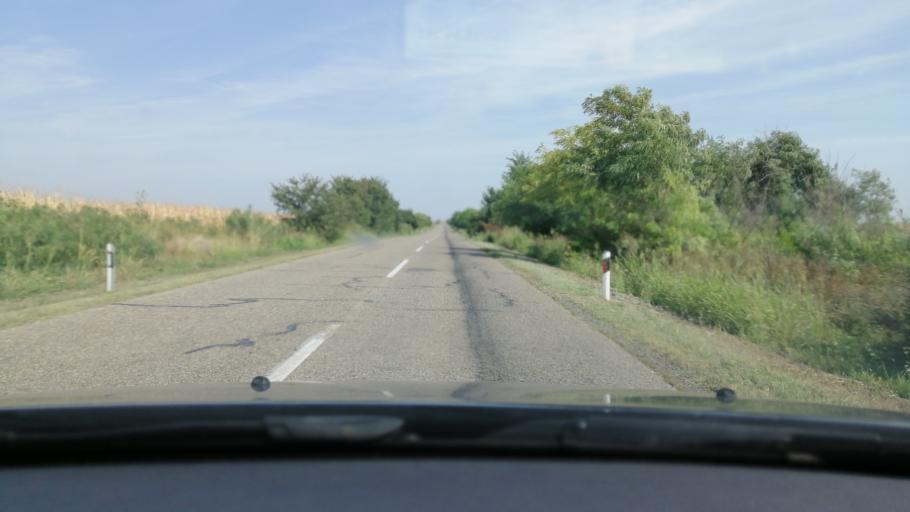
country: RS
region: Autonomna Pokrajina Vojvodina
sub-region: Juznobanatski Okrug
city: Kovacica
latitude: 45.1390
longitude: 20.6163
